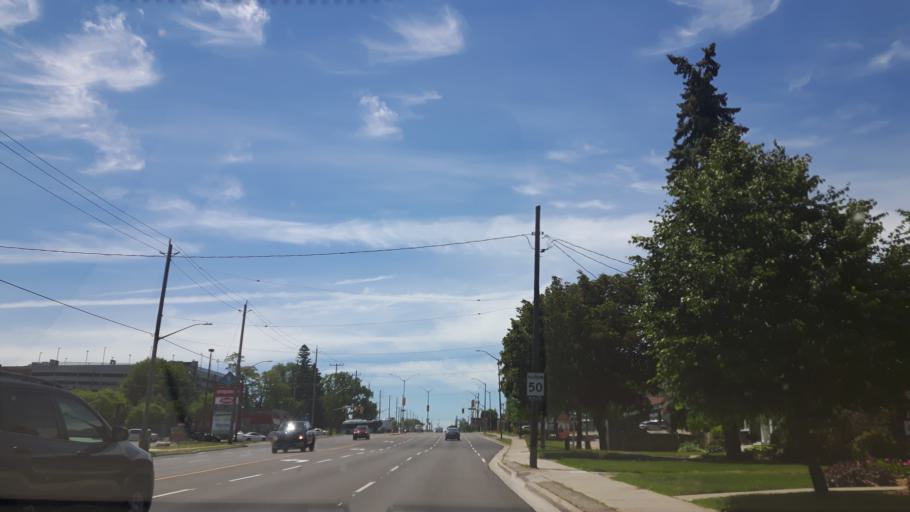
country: CA
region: Ontario
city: London
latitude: 42.9633
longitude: -81.2316
